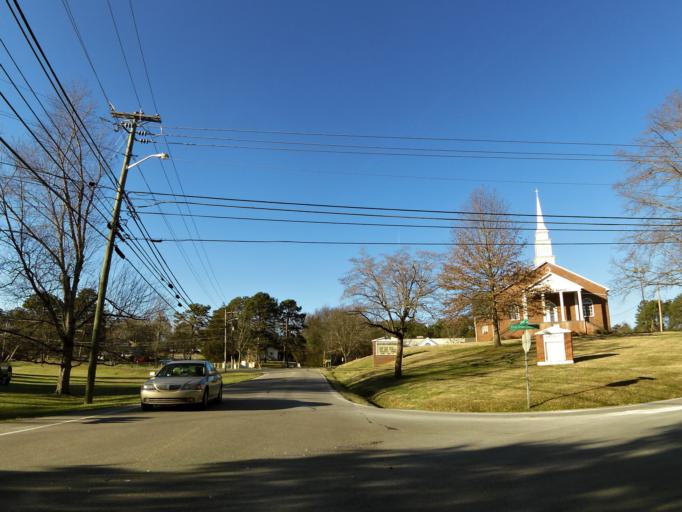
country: US
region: Tennessee
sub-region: Knox County
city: Farragut
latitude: 35.9565
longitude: -84.0496
